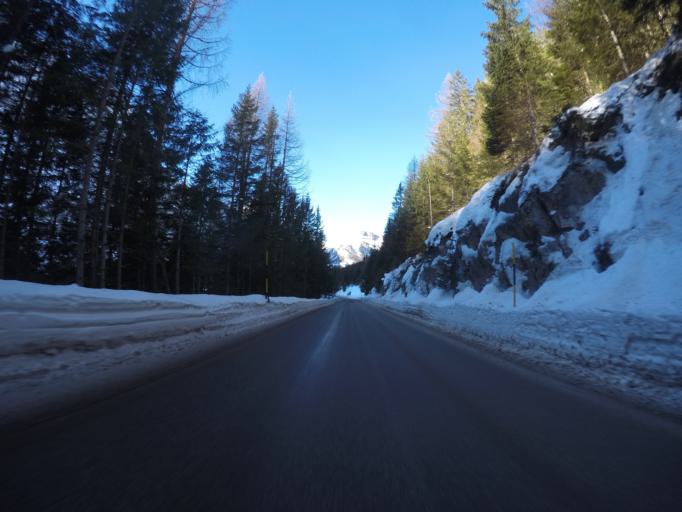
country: IT
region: Trentino-Alto Adige
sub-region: Provincia di Trento
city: Canazei
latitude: 46.4615
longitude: 11.8298
